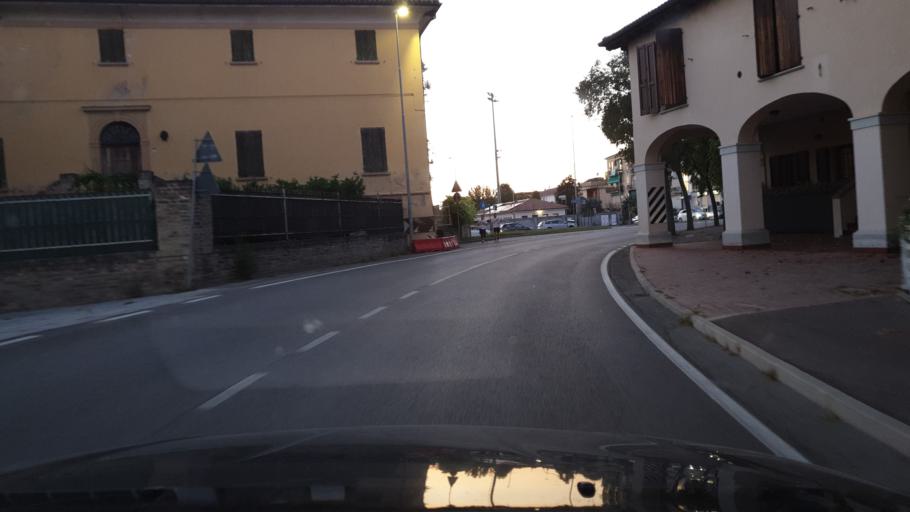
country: IT
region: Emilia-Romagna
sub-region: Provincia di Bologna
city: Altedo
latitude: 44.6626
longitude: 11.4864
